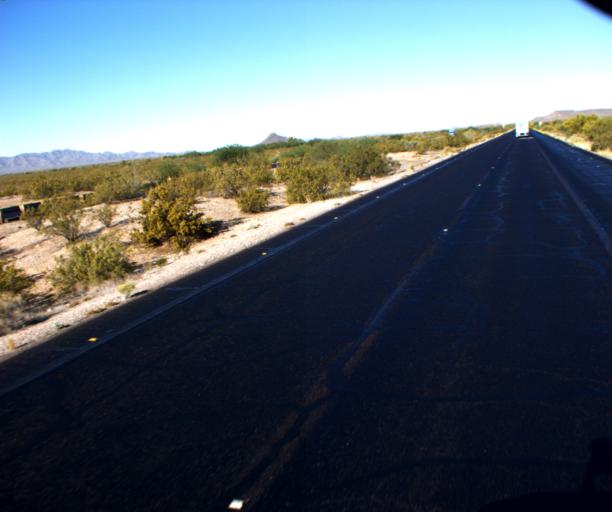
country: US
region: Arizona
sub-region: Pinal County
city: Maricopa
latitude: 32.8428
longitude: -112.2601
